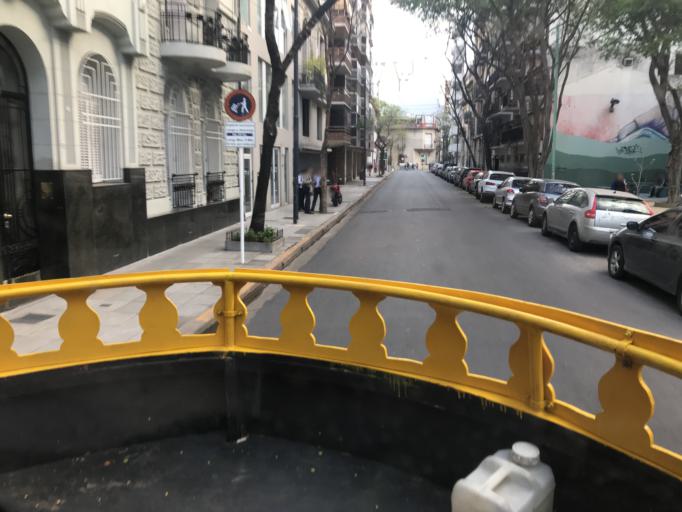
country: AR
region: Buenos Aires F.D.
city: Retiro
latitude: -34.5934
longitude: -58.4086
